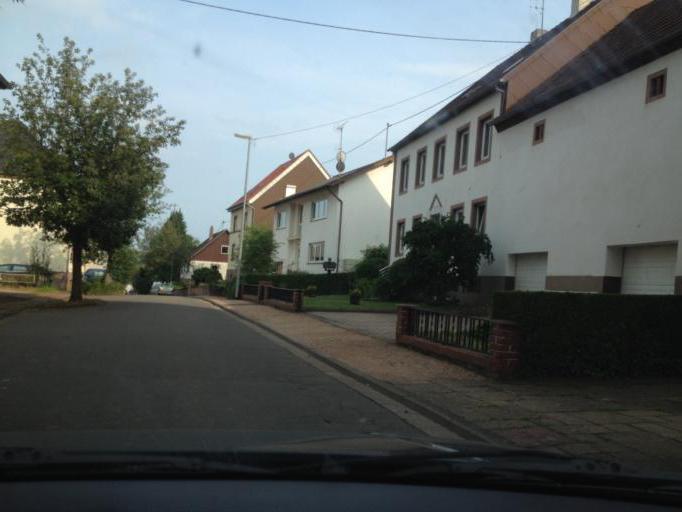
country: DE
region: Saarland
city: Ottweiler
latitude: 49.4325
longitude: 7.1561
